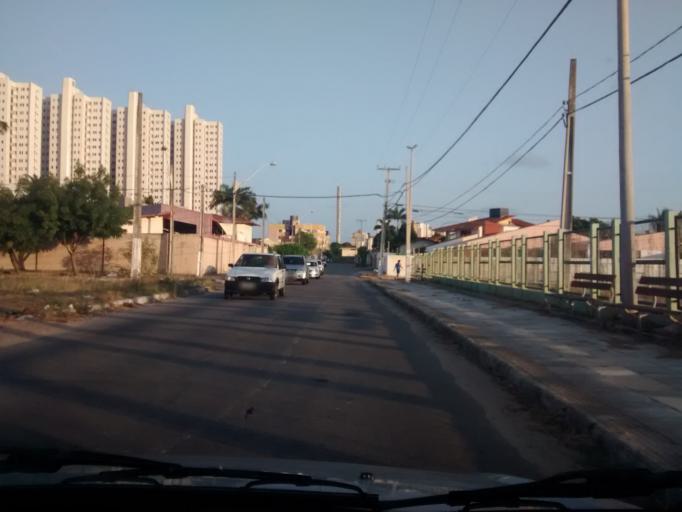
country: BR
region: Rio Grande do Norte
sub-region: Natal
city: Natal
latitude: -5.8664
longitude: -35.1886
